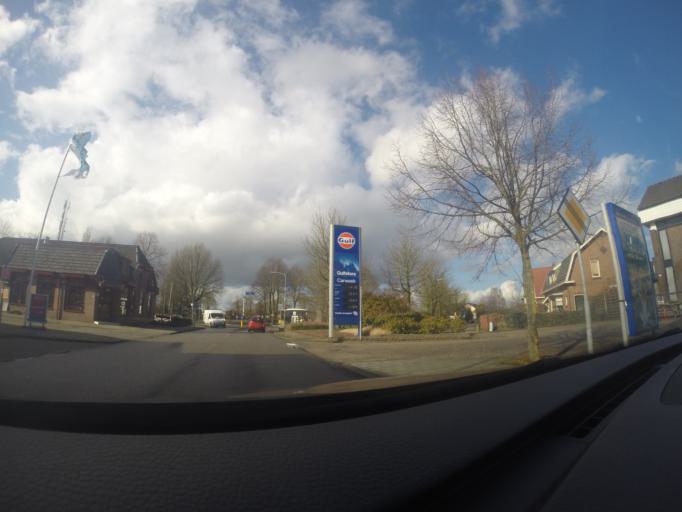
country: NL
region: Gelderland
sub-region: Oude IJsselstreek
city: Varsseveld
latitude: 51.9444
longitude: 6.4577
